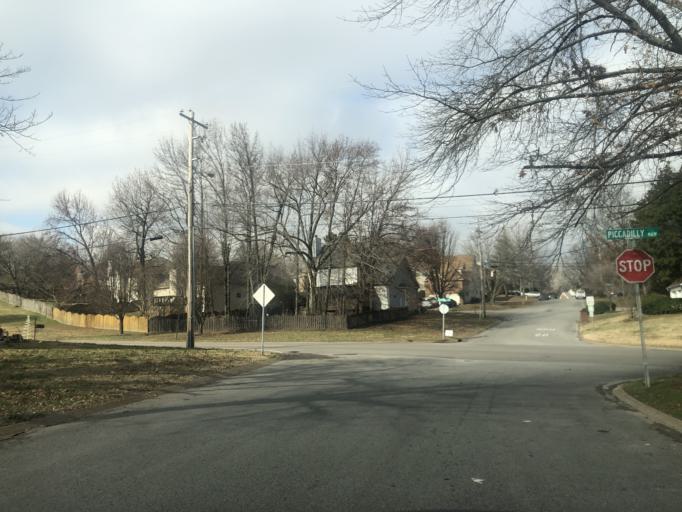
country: US
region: Tennessee
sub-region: Rutherford County
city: La Vergne
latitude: 36.0837
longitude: -86.6560
